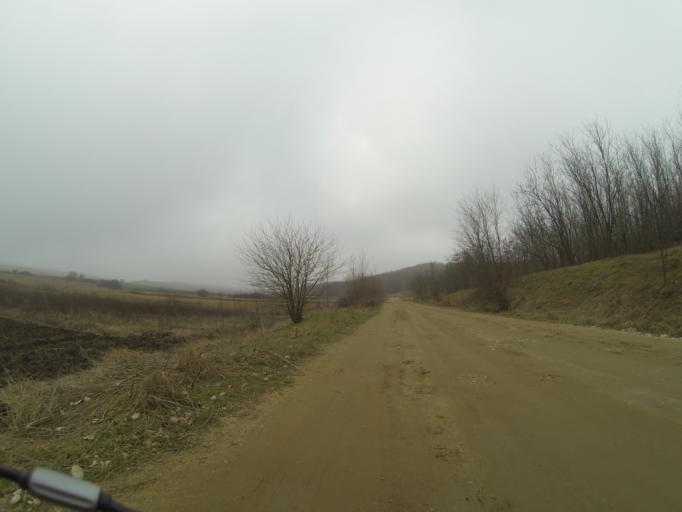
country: RO
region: Mehedinti
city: Padina Mica
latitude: 44.4854
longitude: 23.0297
